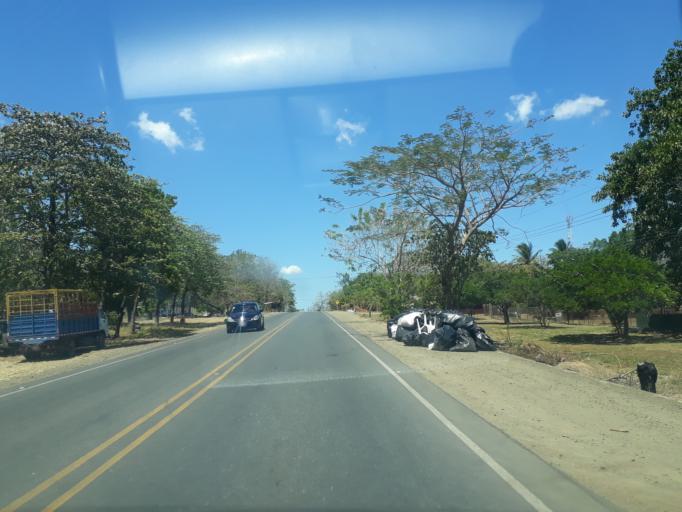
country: CR
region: Guanacaste
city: Liberia
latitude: 10.6623
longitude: -85.4713
